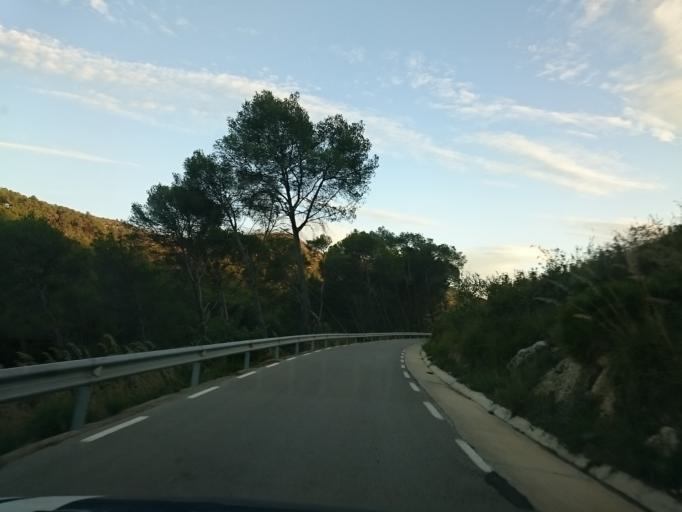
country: ES
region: Catalonia
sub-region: Provincia de Barcelona
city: Olivella
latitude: 41.3109
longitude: 1.7848
